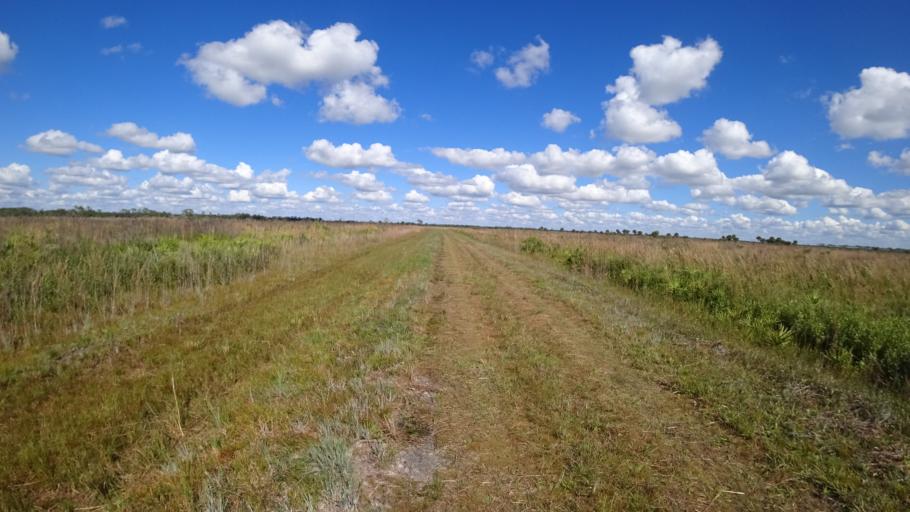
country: US
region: Florida
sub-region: Sarasota County
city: Lake Sarasota
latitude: 27.2635
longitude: -82.2682
